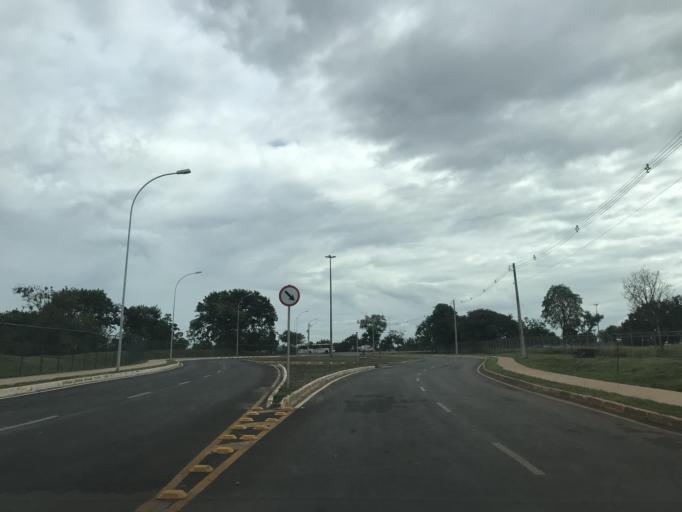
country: BR
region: Federal District
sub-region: Brasilia
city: Brasilia
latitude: -15.7857
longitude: -47.9182
